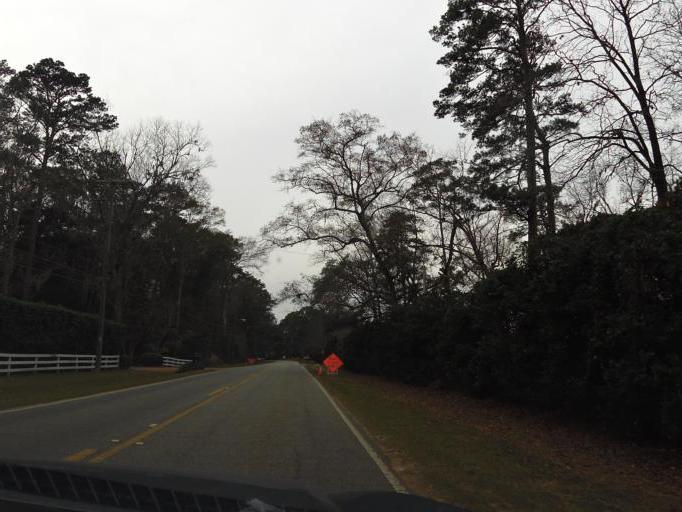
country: US
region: Georgia
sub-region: Thomas County
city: Thomasville
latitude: 30.8131
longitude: -83.9623
